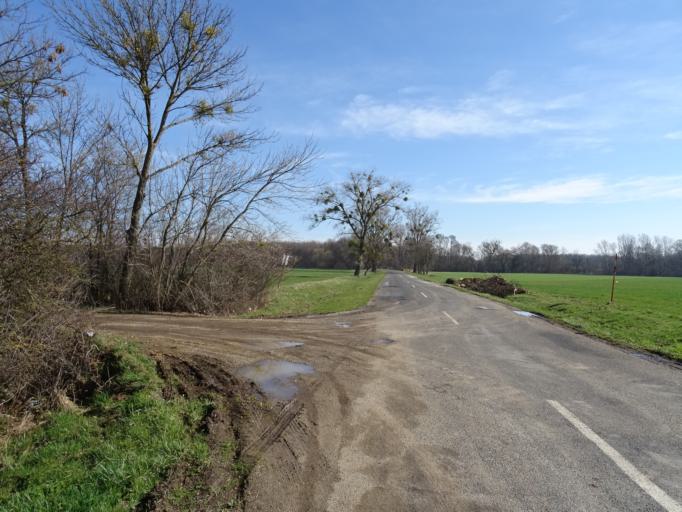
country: HU
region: Gyor-Moson-Sopron
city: Kapuvar
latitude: 47.5257
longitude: 17.0292
